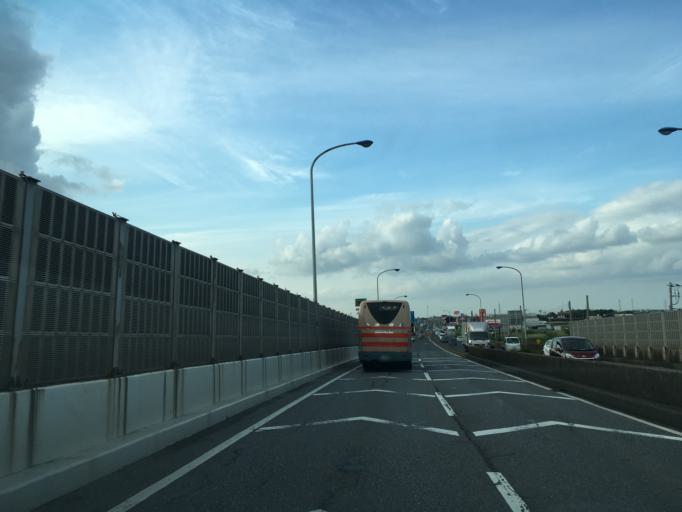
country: JP
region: Chiba
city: Kisarazu
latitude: 35.3919
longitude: 139.9408
